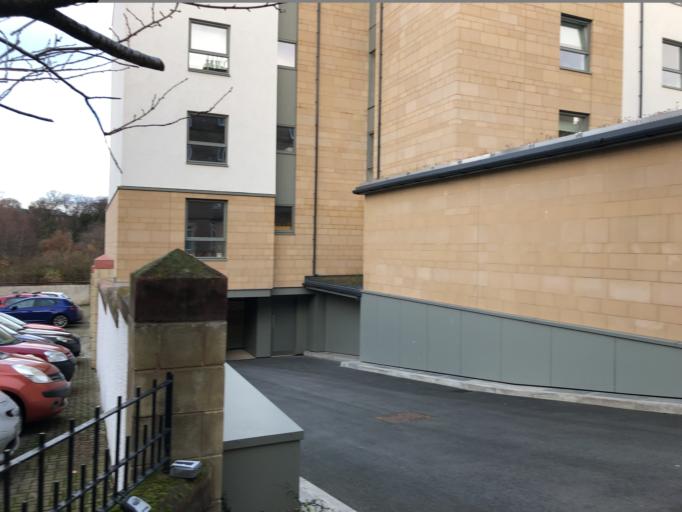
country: GB
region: Scotland
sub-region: West Lothian
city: Seafield
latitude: 55.9581
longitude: -3.1607
